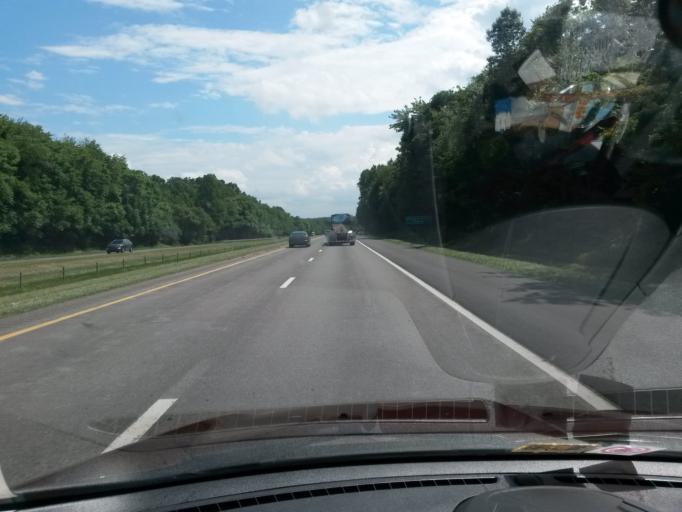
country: US
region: North Carolina
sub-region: Surry County
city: Dobson
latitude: 36.3842
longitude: -80.7895
